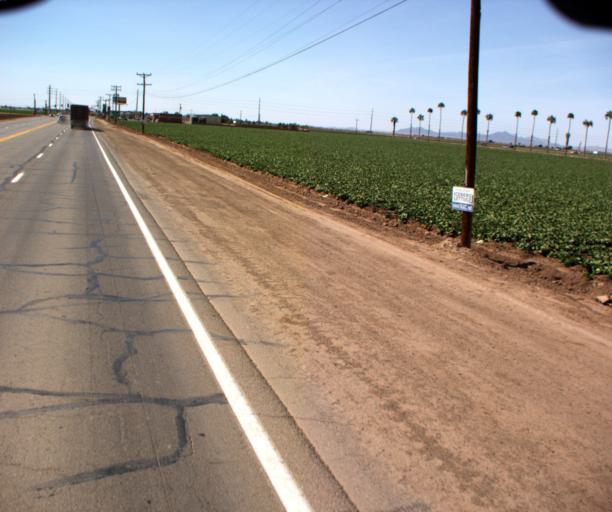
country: US
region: Arizona
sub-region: Yuma County
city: Fortuna Foothills
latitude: 32.6993
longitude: -114.5088
